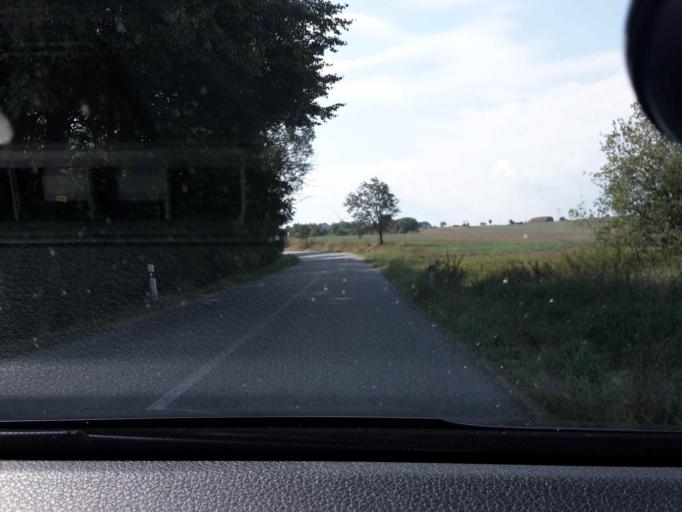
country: CZ
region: Vysocina
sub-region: Okres Jihlava
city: Trest'
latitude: 49.2705
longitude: 15.5747
